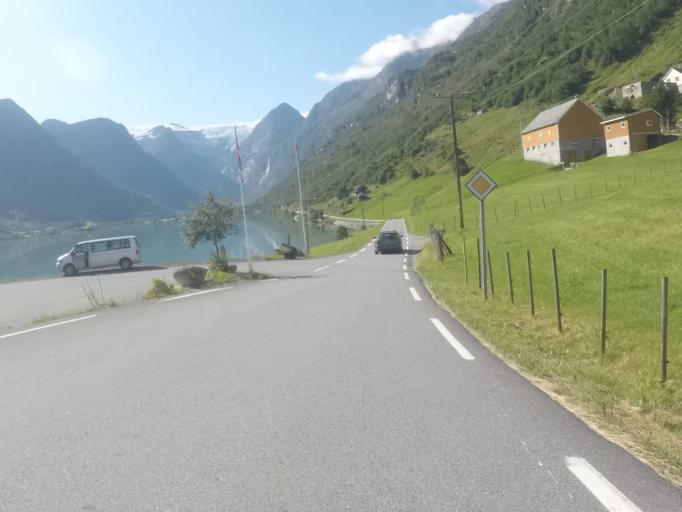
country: NO
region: Sogn og Fjordane
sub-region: Stryn
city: Stryn
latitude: 61.7230
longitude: 6.7944
